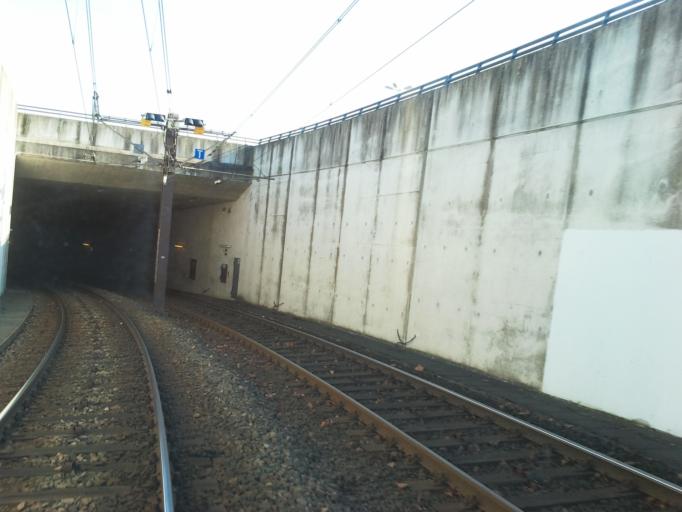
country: DE
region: Mecklenburg-Vorpommern
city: Rostock
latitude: 54.0778
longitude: 12.1285
